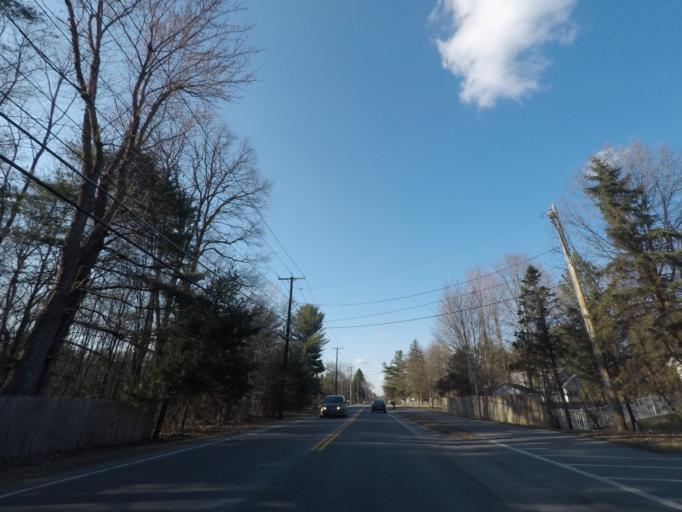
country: US
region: New York
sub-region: Saratoga County
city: Country Knolls
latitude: 42.8501
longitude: -73.7943
